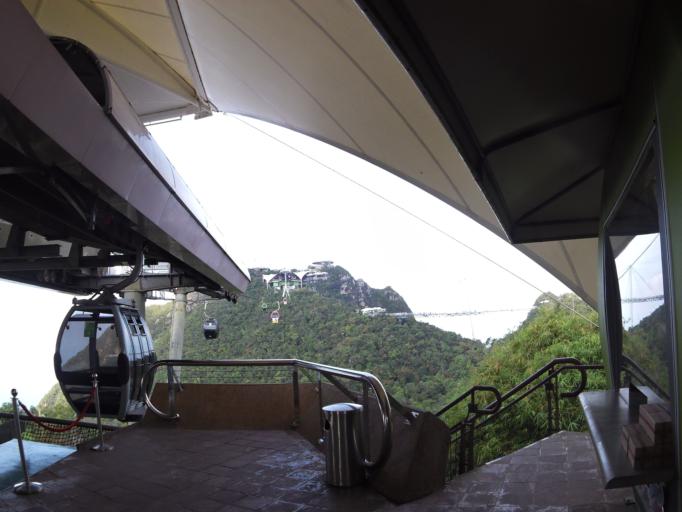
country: MY
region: Kedah
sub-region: Langkawi
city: Kuah
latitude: 6.3853
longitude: 99.6650
